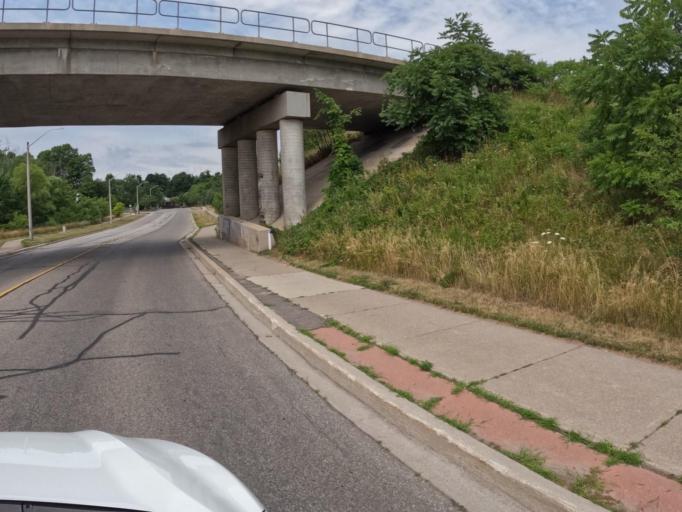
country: CA
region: Ontario
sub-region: Halton
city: Milton
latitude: 43.6432
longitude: -79.9351
